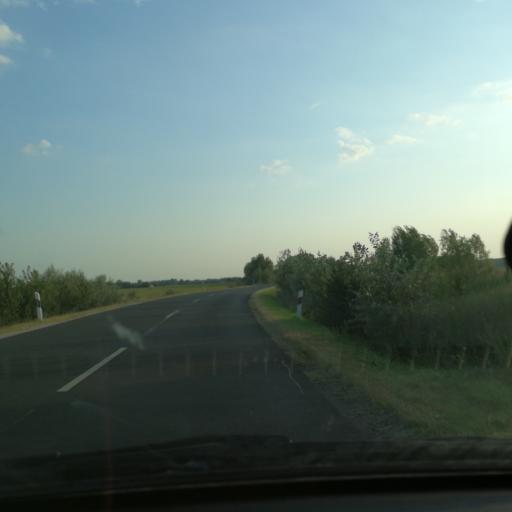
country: HU
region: Bacs-Kiskun
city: Kiskunmajsa
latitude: 46.4767
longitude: 19.7068
